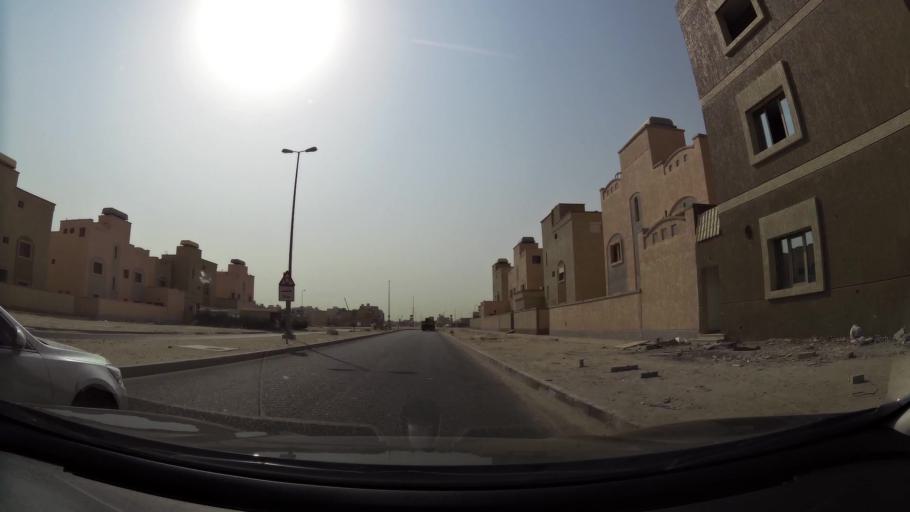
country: KW
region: Muhafazat al Jahra'
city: Al Jahra'
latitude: 29.3560
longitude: 47.7568
